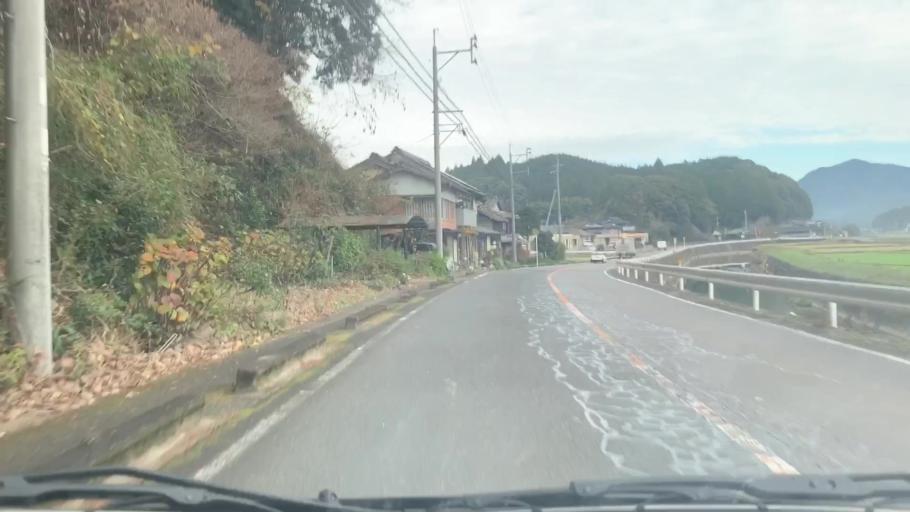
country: JP
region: Saga Prefecture
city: Takeocho-takeo
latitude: 33.2281
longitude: 129.9638
